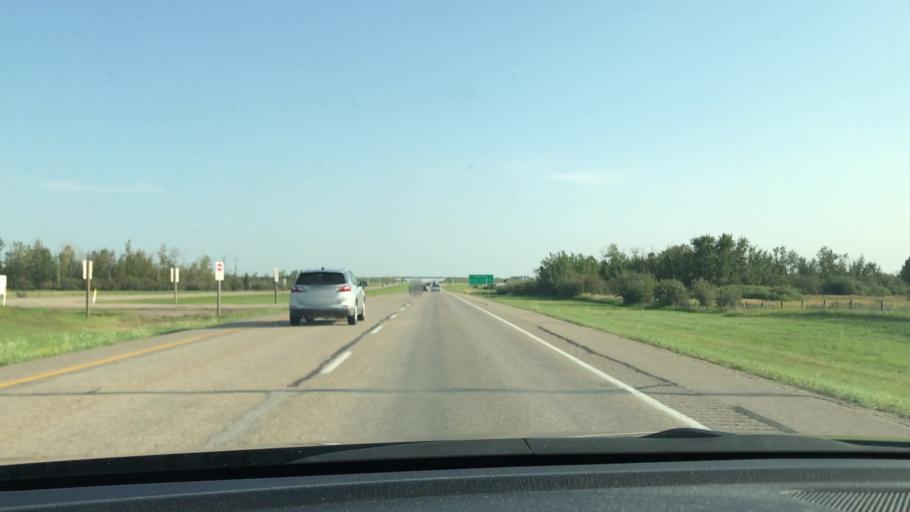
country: CA
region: Alberta
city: Millet
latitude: 53.1007
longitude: -113.5984
